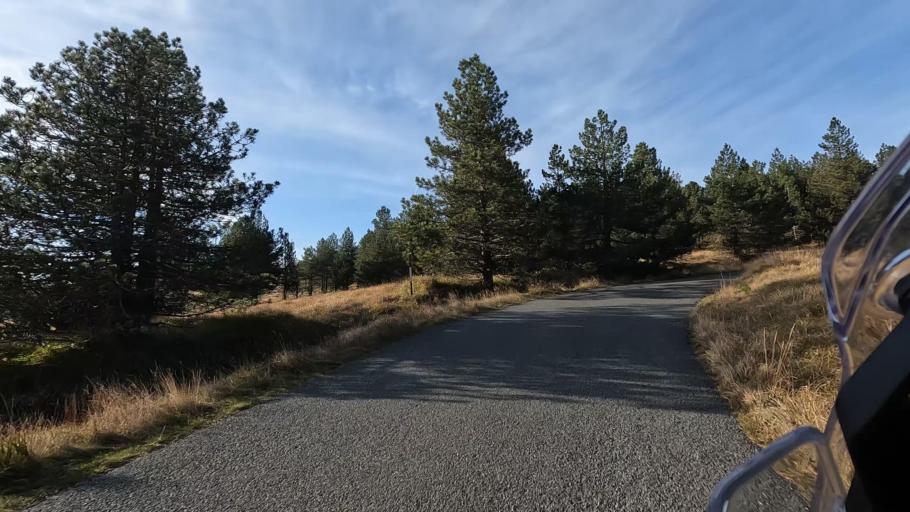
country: IT
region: Liguria
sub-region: Provincia di Genova
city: Sciarborasca
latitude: 44.4308
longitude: 8.5723
